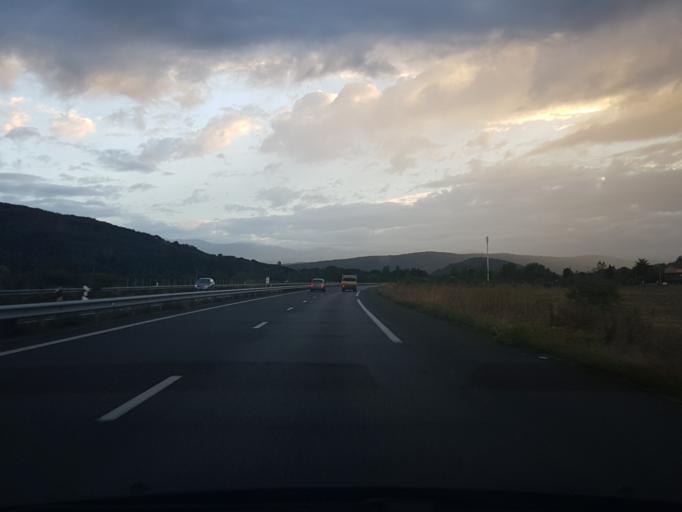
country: FR
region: Midi-Pyrenees
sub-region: Departement de l'Ariege
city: Varilhes
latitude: 43.0432
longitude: 1.6429
